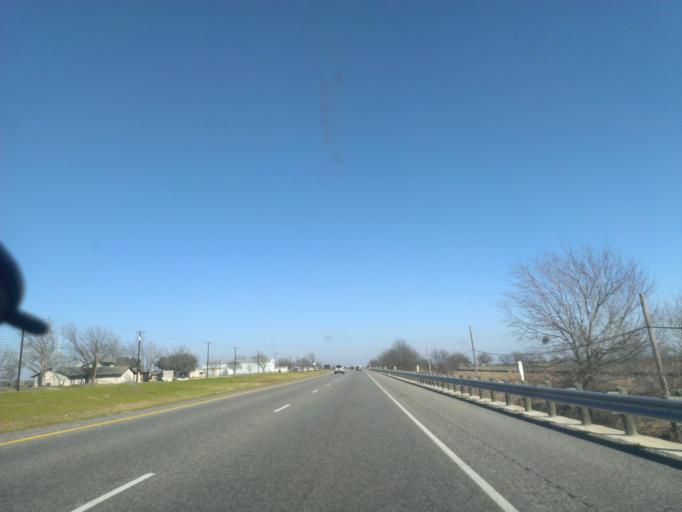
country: US
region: Texas
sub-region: Williamson County
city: Taylor
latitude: 30.5810
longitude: -97.3492
